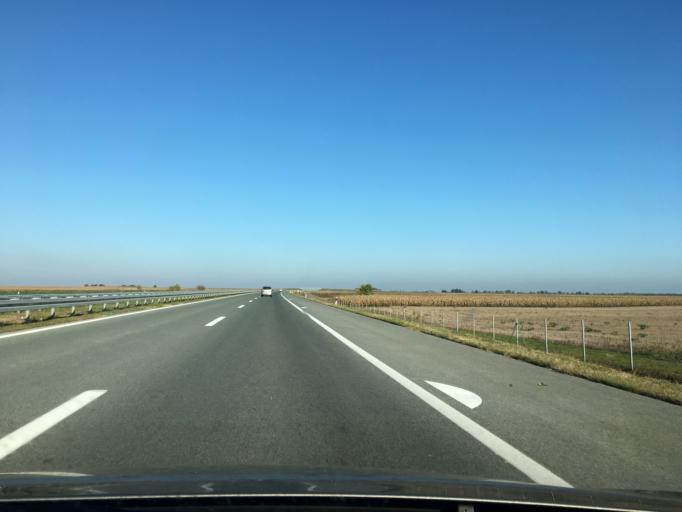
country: RS
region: Autonomna Pokrajina Vojvodina
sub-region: Severnobacki Okrug
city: Mali Igos
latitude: 45.7347
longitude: 19.7043
